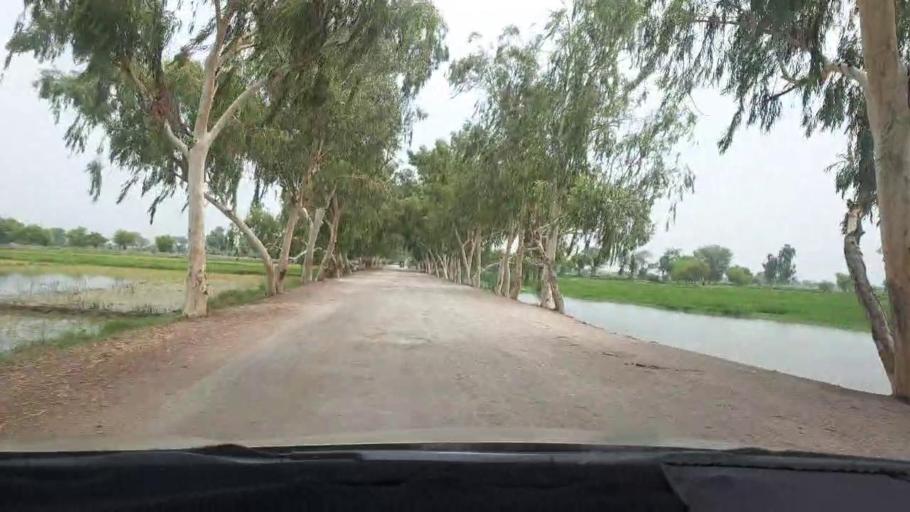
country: PK
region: Sindh
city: Ratodero
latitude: 27.7624
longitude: 68.3219
